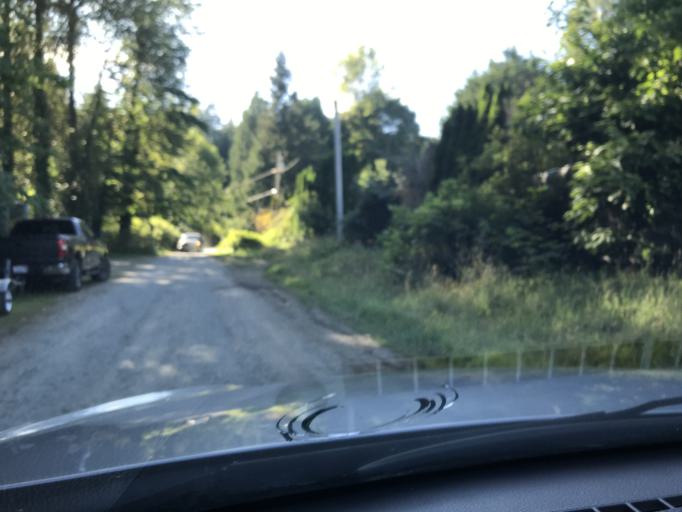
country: US
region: Washington
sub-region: King County
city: Maple Heights-Lake Desire
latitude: 47.4369
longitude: -122.0934
